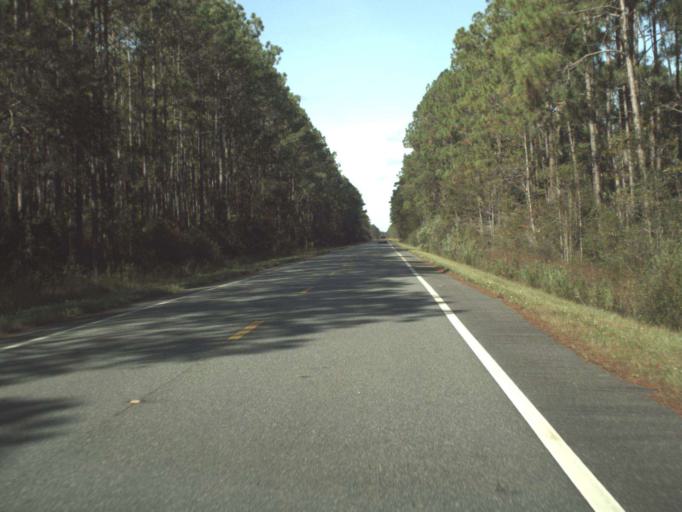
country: US
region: Florida
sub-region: Franklin County
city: Eastpoint
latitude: 29.8395
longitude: -84.9411
